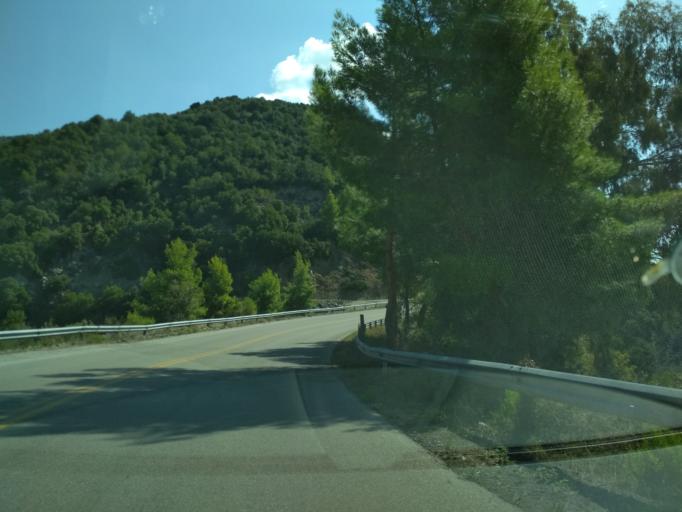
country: GR
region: Central Greece
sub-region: Nomos Evvoias
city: Roviai
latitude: 38.8529
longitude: 23.1393
